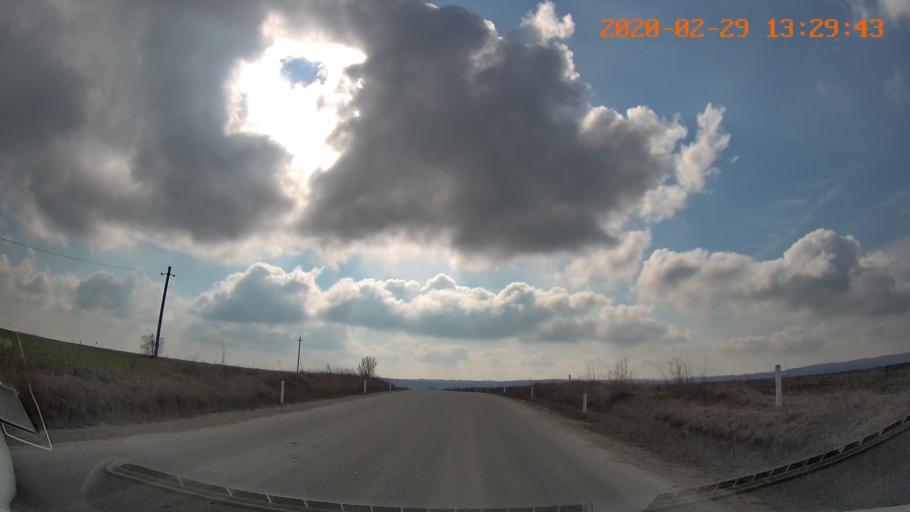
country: MD
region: Telenesti
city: Camenca
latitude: 47.8940
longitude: 28.6342
